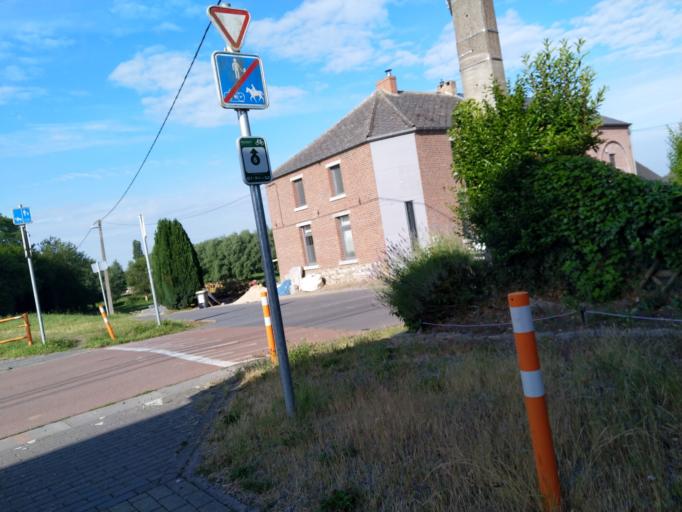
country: BE
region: Wallonia
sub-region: Province du Hainaut
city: Estinnes-au-Val
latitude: 50.3648
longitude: 4.1145
